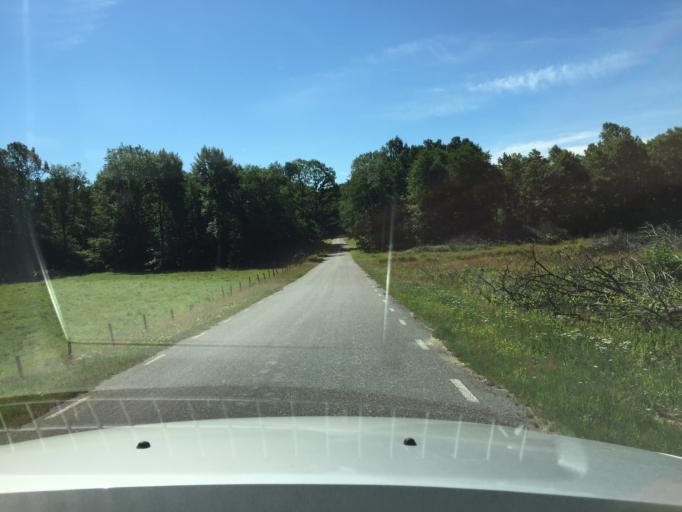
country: SE
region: Skane
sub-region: Hassleholms Kommun
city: Sosdala
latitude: 56.0236
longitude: 13.5806
